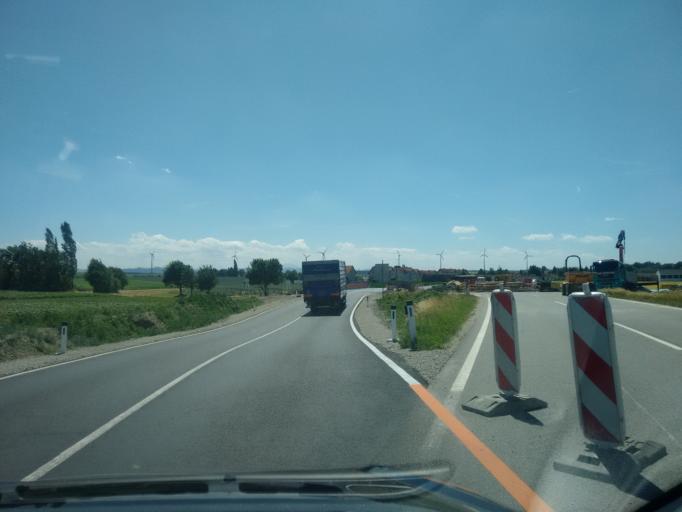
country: AT
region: Lower Austria
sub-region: Politischer Bezirk Sankt Polten
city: Haunoldstein
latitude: 48.1965
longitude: 15.4666
